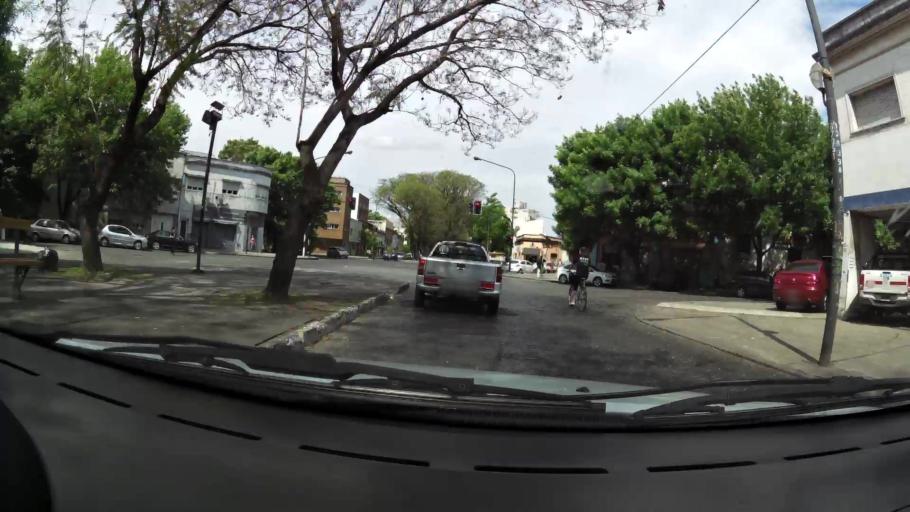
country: AR
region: Buenos Aires
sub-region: Partido de La Plata
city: La Plata
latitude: -34.9208
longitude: -57.9376
